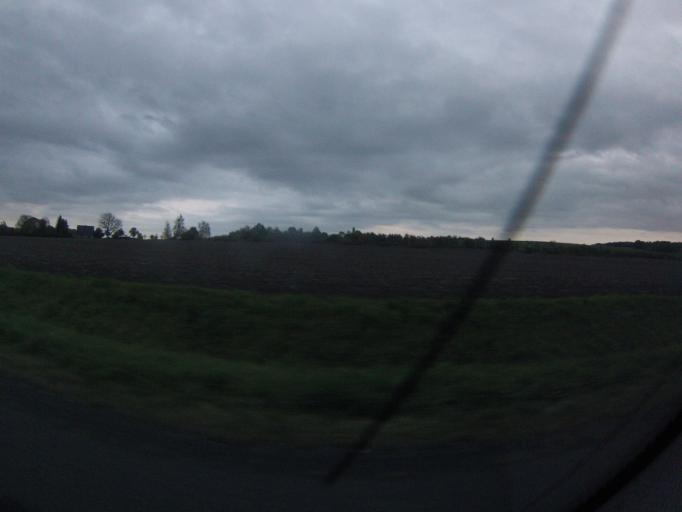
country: DE
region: Thuringia
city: Saara
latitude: 50.9297
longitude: 12.4190
